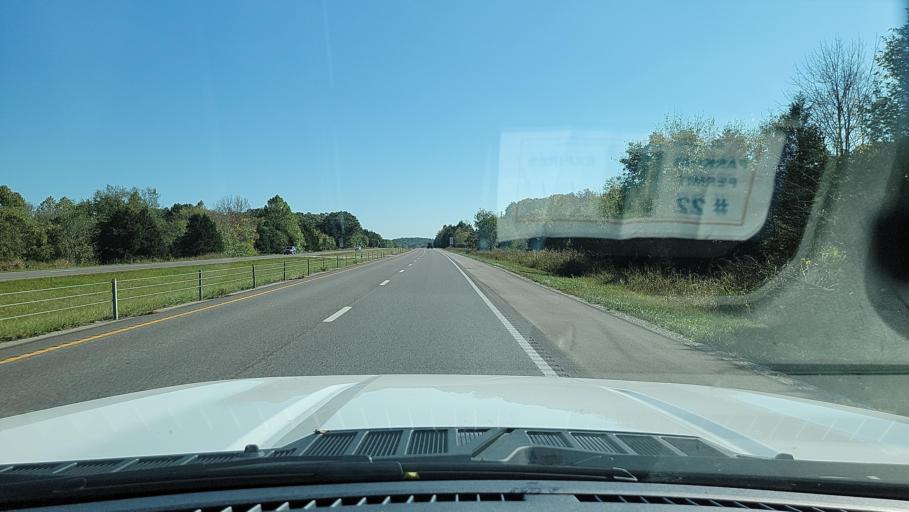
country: US
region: Missouri
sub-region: Jefferson County
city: Crystal City
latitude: 38.0865
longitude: -90.2986
